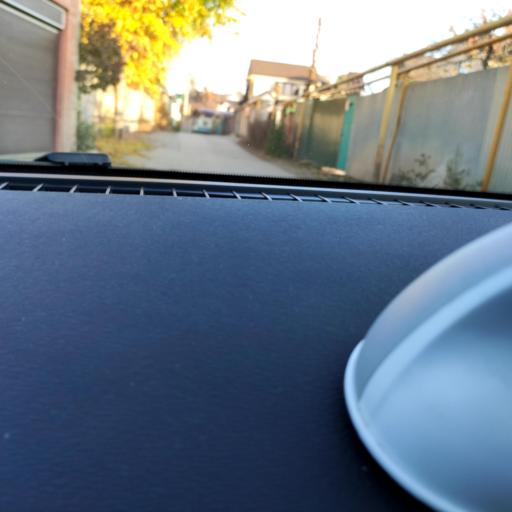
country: RU
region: Samara
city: Samara
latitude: 53.2274
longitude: 50.1600
